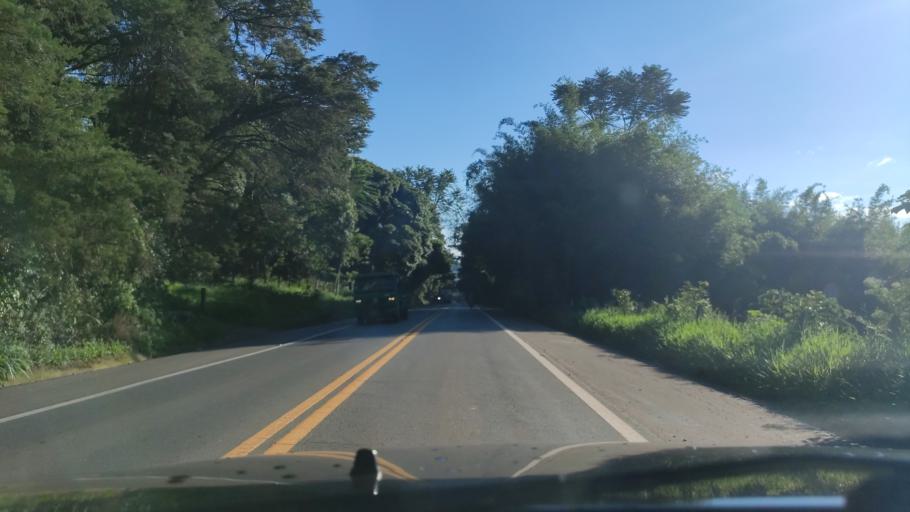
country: BR
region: Sao Paulo
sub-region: Socorro
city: Socorro
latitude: -22.5642
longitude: -46.5478
